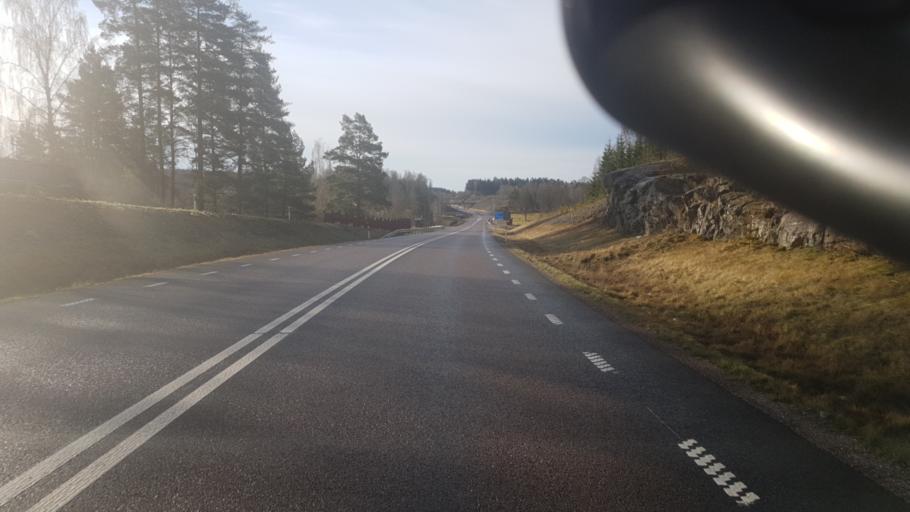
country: SE
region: Vaermland
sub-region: Eda Kommun
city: Amotfors
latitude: 59.7825
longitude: 12.3617
